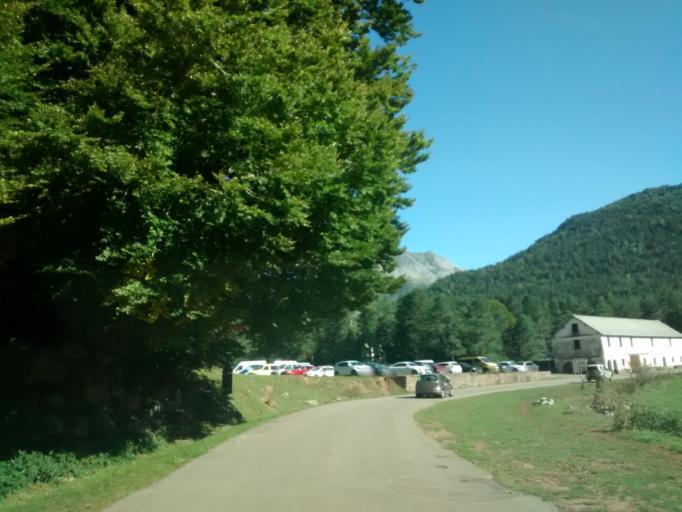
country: ES
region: Aragon
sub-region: Provincia de Huesca
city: Aragues del Puerto
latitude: 42.8310
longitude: -0.7124
